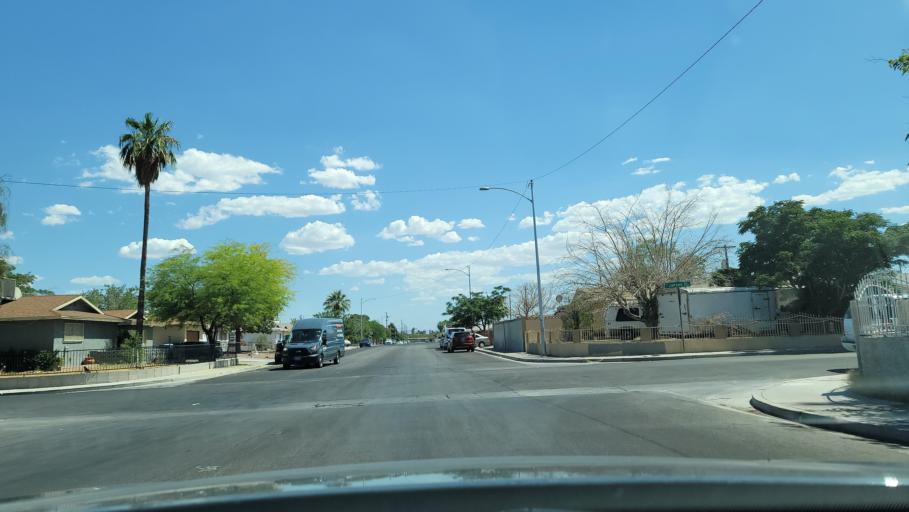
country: US
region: Nevada
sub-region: Clark County
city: North Las Vegas
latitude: 36.1826
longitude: -115.1206
